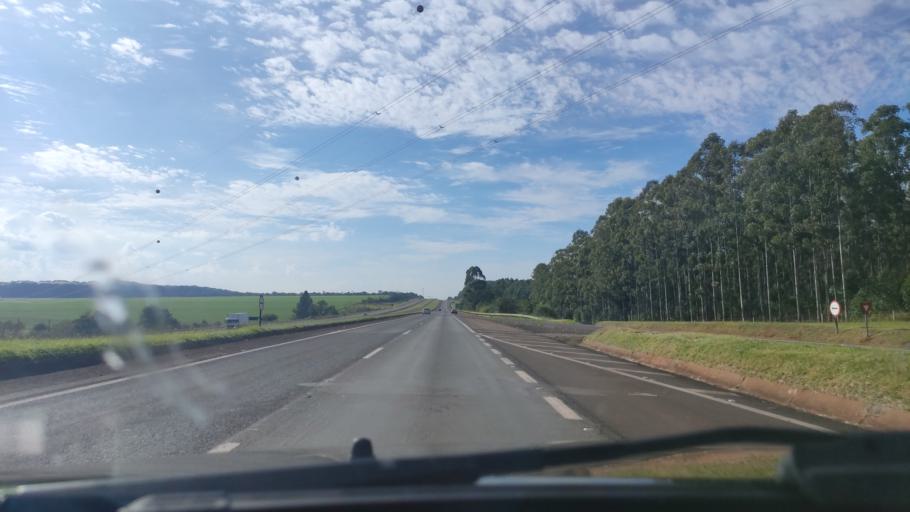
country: BR
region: Sao Paulo
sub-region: Itatinga
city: Itatinga
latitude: -23.0112
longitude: -48.7030
